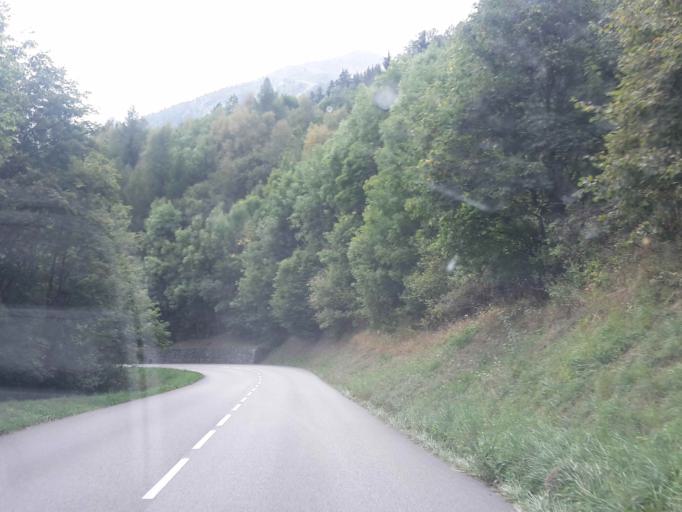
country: FR
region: Rhone-Alpes
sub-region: Departement de la Savoie
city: Saint-Michel-de-Maurienne
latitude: 45.1992
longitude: 6.4673
